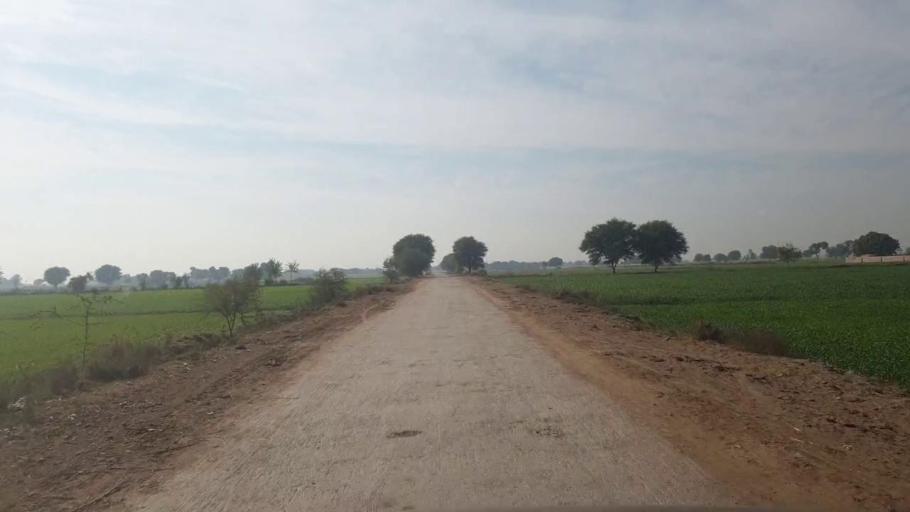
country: PK
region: Sindh
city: Shahpur Chakar
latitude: 26.1806
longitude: 68.5856
